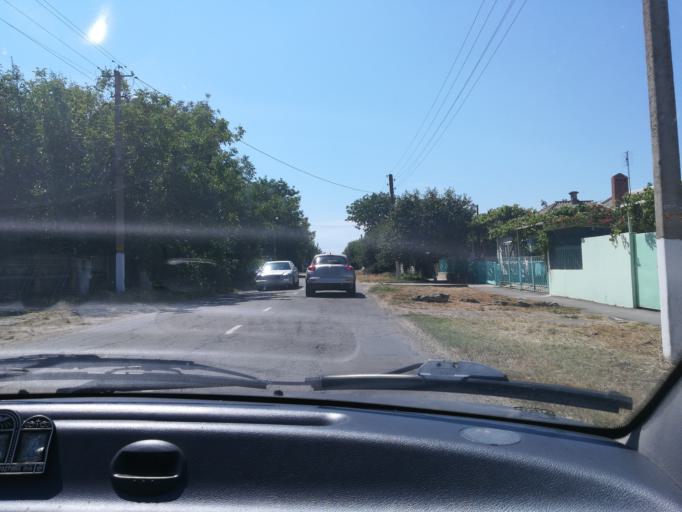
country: RU
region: Krasnodarskiy
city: Blagovetschenskaya
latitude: 45.0561
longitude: 37.1270
